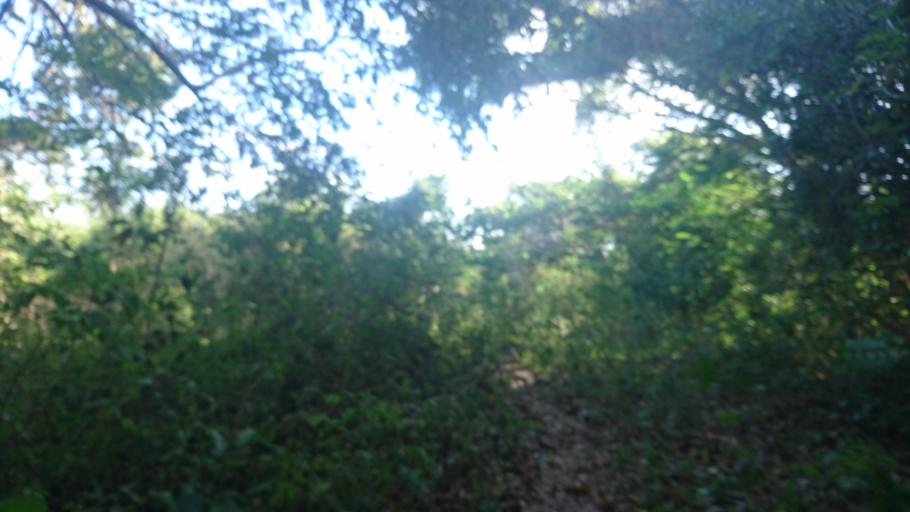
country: CU
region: Artemisa
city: Soroa
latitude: 22.8281
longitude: -82.9212
